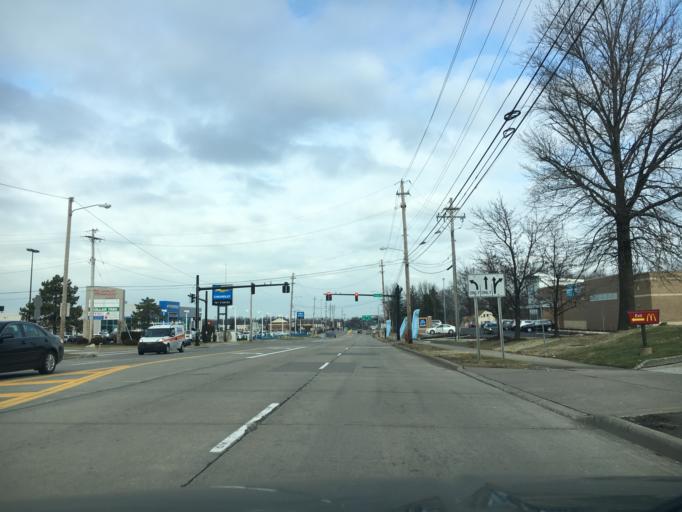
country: US
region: Ohio
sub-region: Cuyahoga County
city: Highland Heights
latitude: 41.5849
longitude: -81.4797
